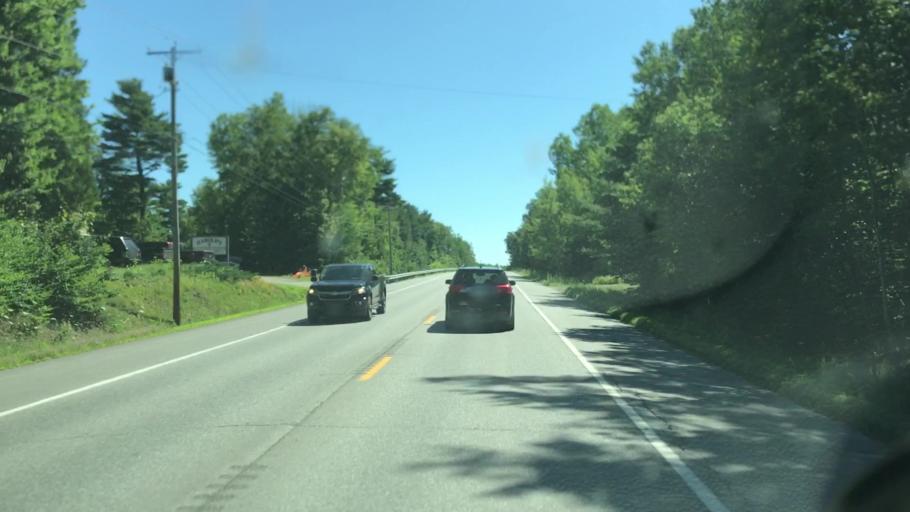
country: US
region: Maine
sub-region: Penobscot County
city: Holden
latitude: 44.7548
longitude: -68.6740
